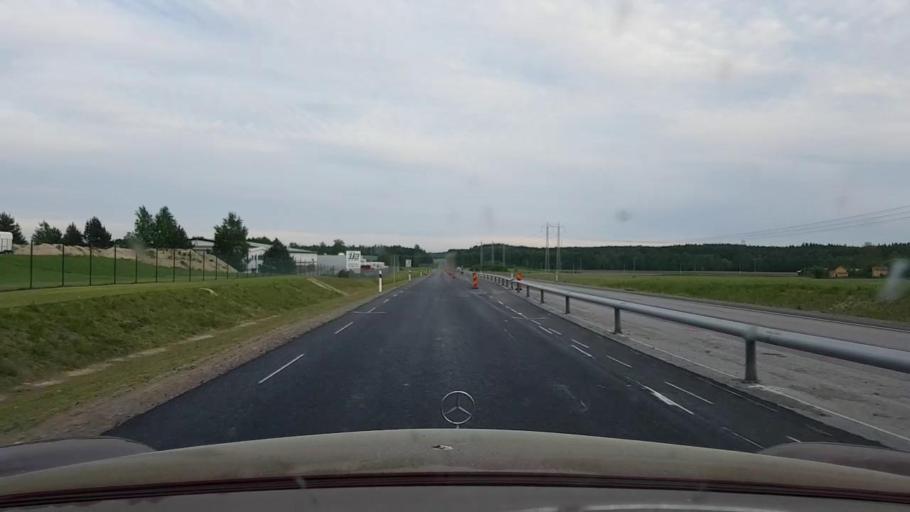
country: SE
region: OErebro
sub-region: Askersunds Kommun
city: Asbro
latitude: 59.0013
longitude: 15.0434
